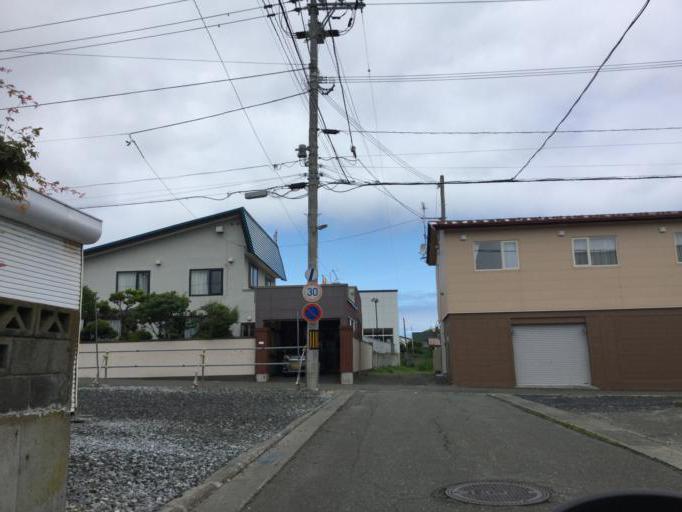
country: JP
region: Hokkaido
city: Wakkanai
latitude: 45.4228
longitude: 141.6729
